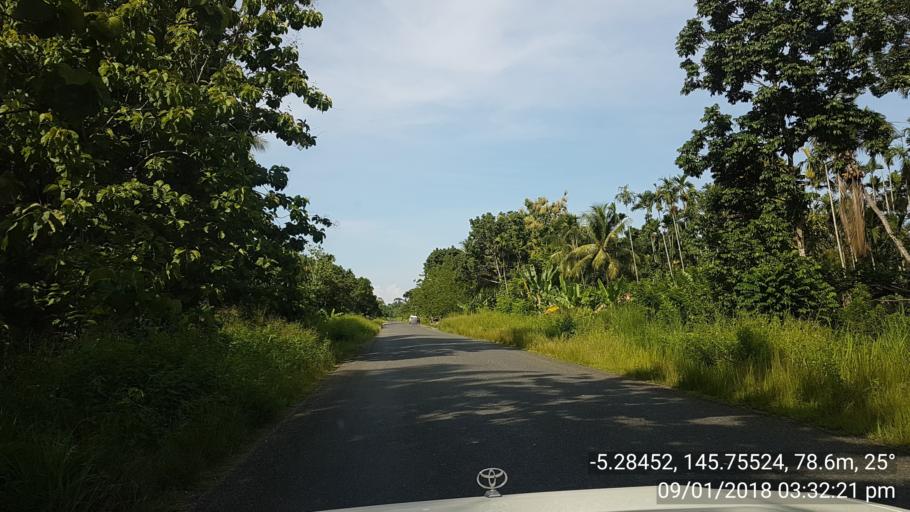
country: PG
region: Madang
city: Madang
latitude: -5.2847
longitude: 145.7552
